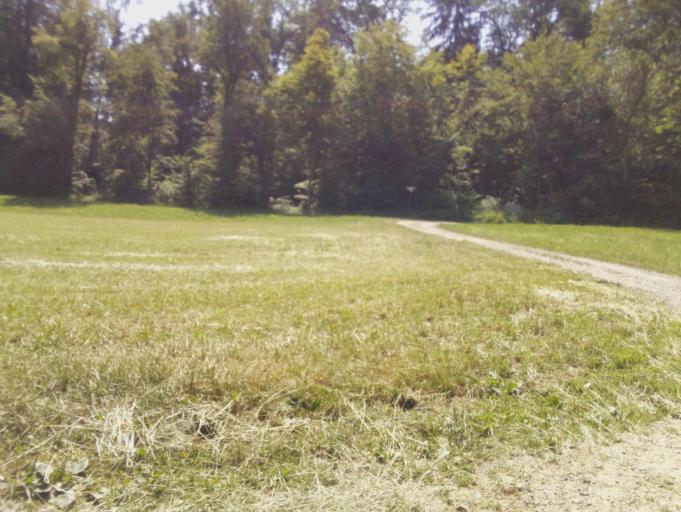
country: CH
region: Zurich
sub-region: Bezirk Andelfingen
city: Kleinandelfingen
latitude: 47.6206
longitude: 8.7038
